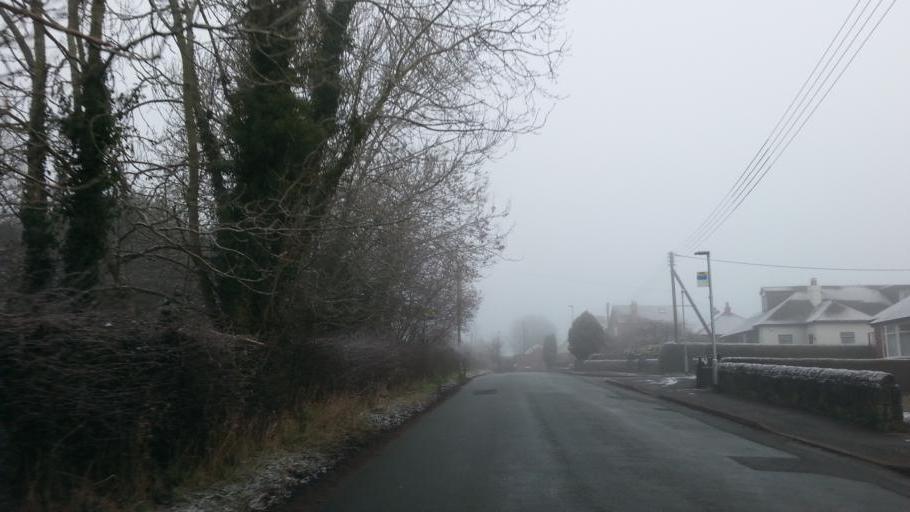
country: GB
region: England
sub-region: Staffordshire
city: Biddulph
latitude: 53.1239
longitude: -2.1802
